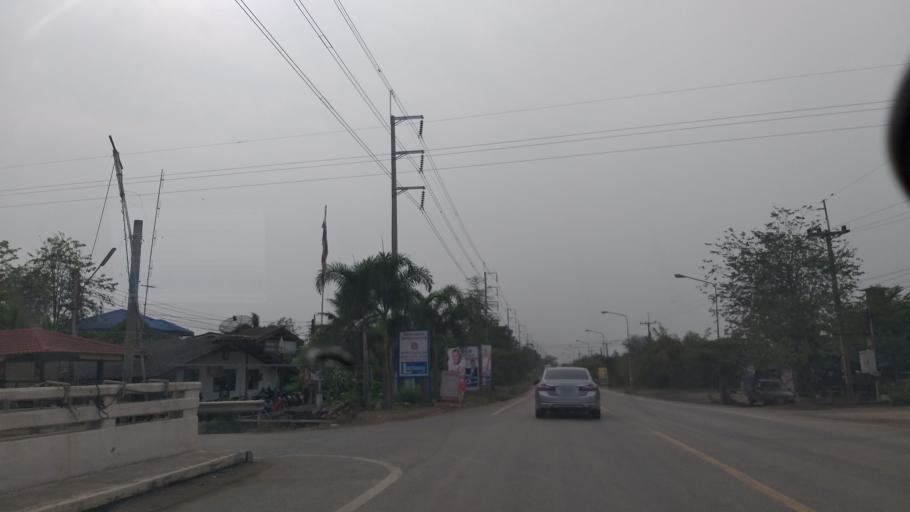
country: TH
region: Chachoengsao
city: Plaeng Yao
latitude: 13.5846
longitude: 101.2200
